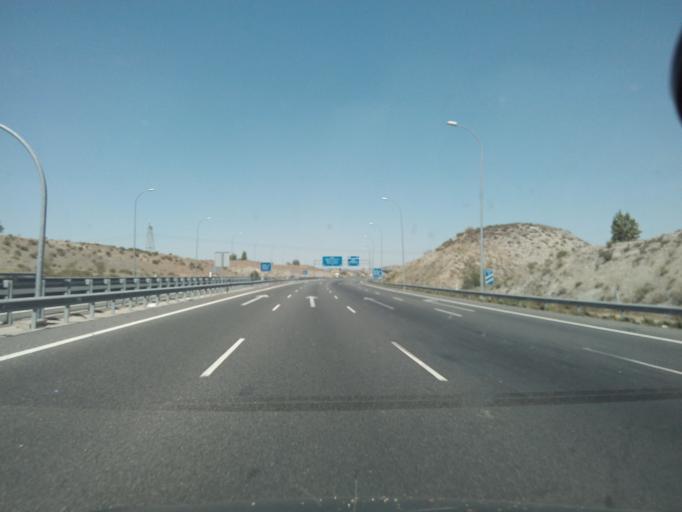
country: ES
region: Madrid
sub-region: Provincia de Madrid
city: Villa de Vallecas
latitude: 40.3280
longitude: -3.6385
